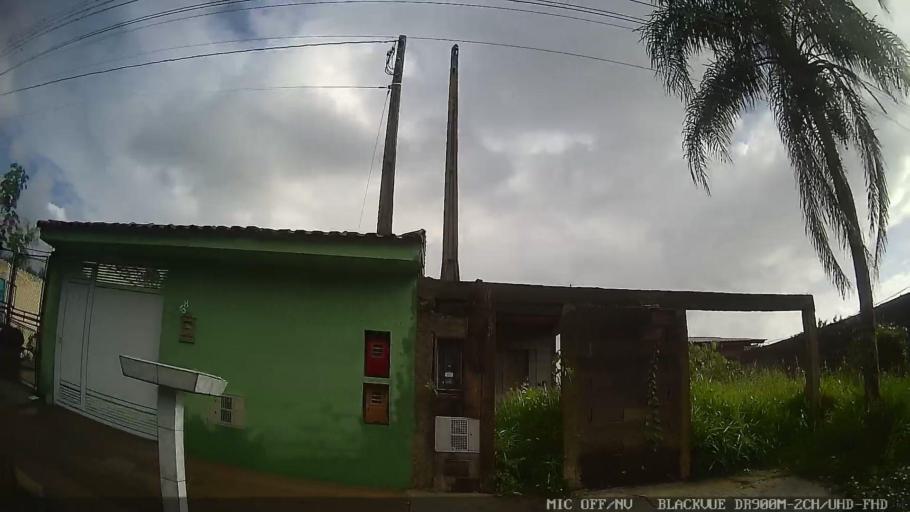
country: BR
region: Sao Paulo
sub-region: Itanhaem
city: Itanhaem
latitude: -24.1951
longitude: -46.8223
